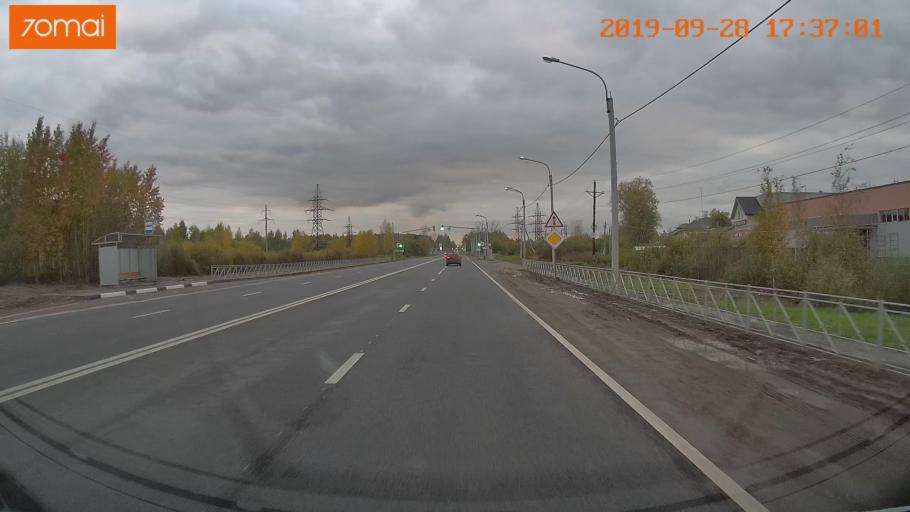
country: RU
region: Jaroslavl
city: Yaroslavl
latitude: 57.5421
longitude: 39.9607
